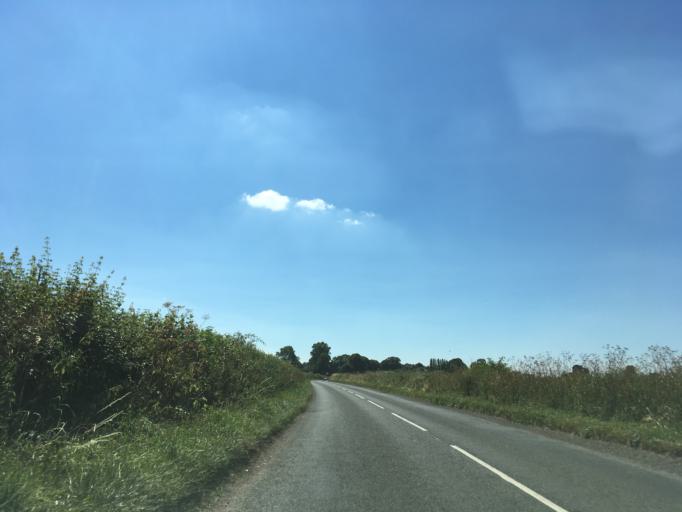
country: GB
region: England
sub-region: South Gloucestershire
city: Marshfield
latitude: 51.5118
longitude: -2.3272
